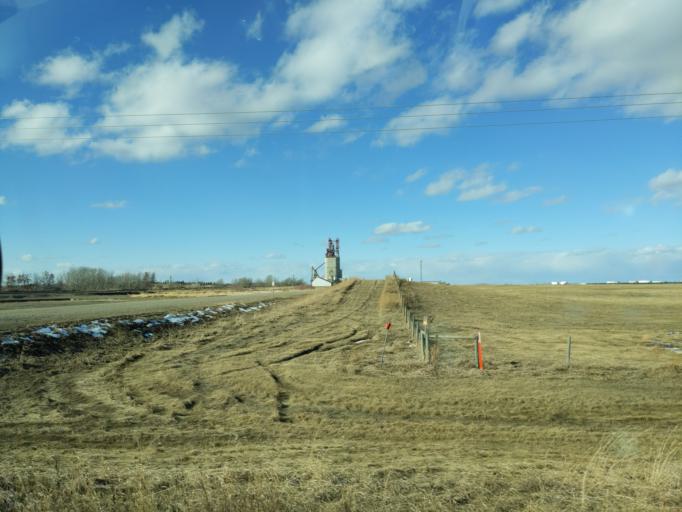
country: CA
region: Saskatchewan
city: Lloydminster
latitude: 53.2489
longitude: -109.9650
